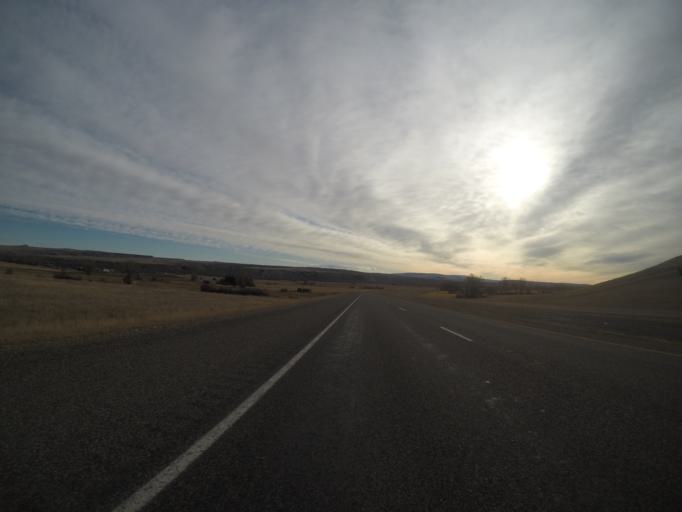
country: US
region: Montana
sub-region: Yellowstone County
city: Laurel
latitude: 45.5428
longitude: -108.8573
